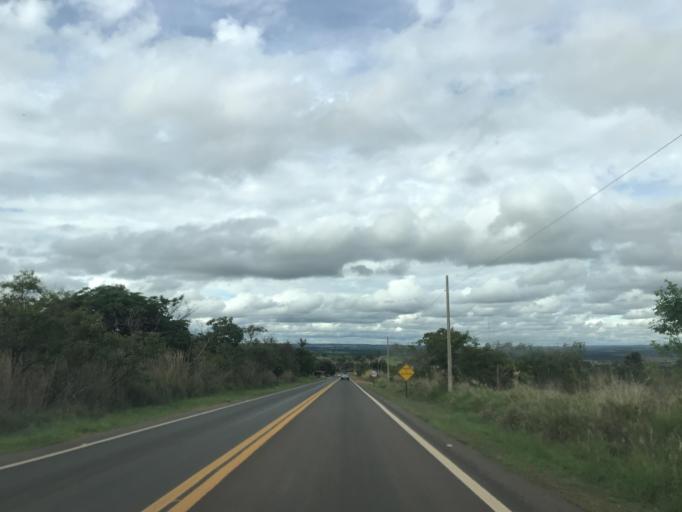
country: BR
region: Goias
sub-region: Piracanjuba
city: Piracanjuba
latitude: -17.2071
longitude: -48.7062
